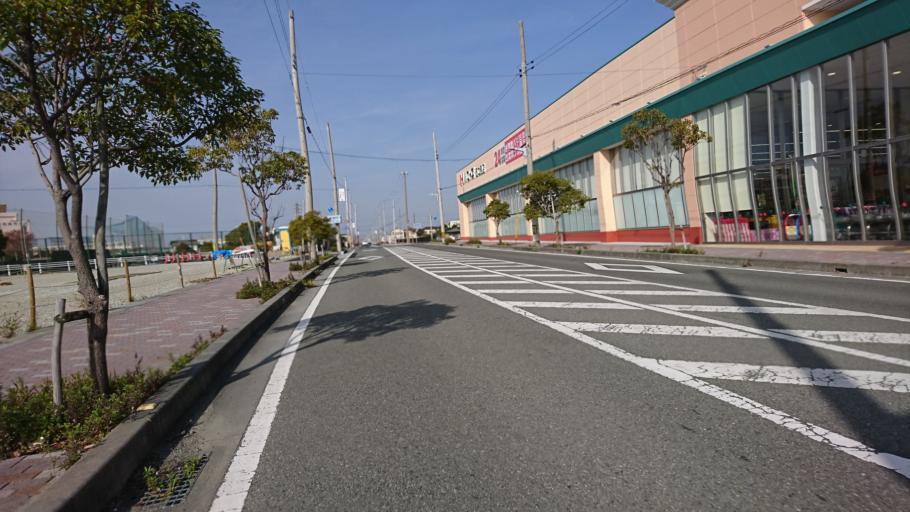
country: JP
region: Hyogo
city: Kakogawacho-honmachi
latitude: 34.7064
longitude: 134.8748
